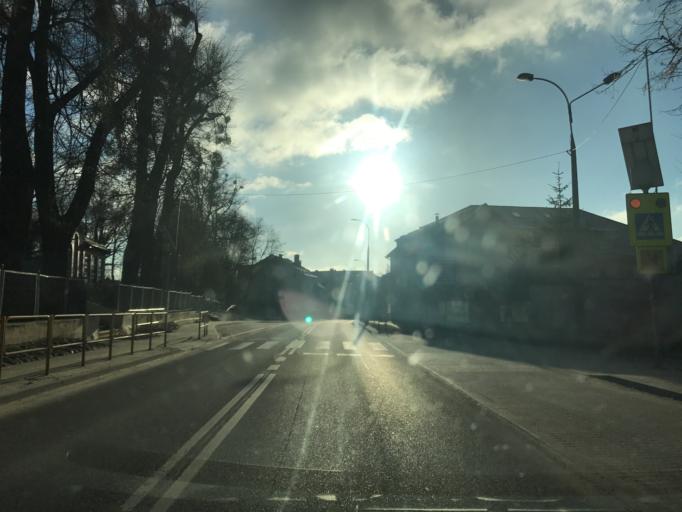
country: PL
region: Warmian-Masurian Voivodeship
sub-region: Powiat ostrodzki
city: Ostroda
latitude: 53.7050
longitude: 19.9613
